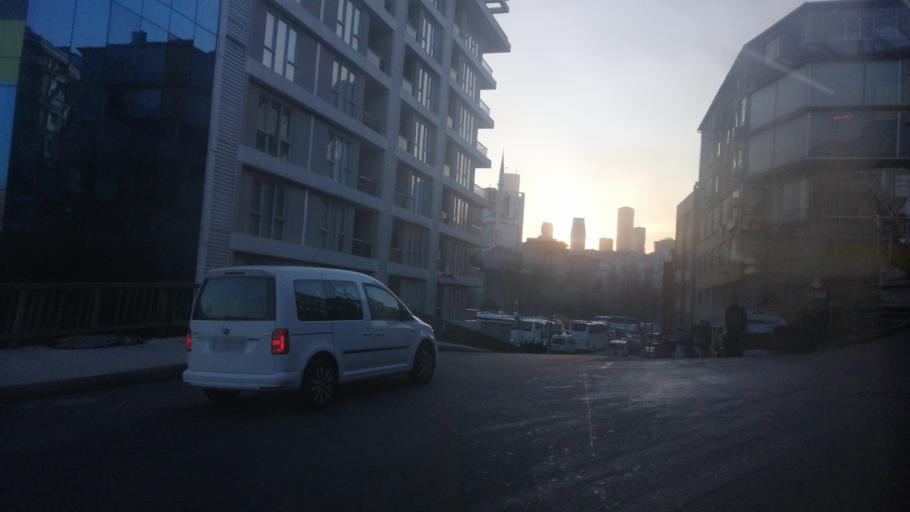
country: TR
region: Istanbul
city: Sisli
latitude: 41.0879
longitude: 28.9846
